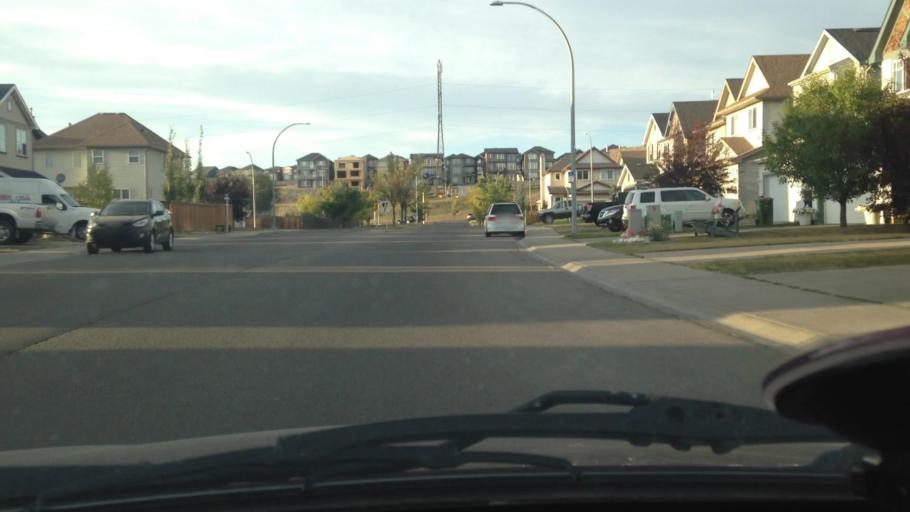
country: CA
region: Alberta
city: Calgary
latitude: 51.1661
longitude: -114.1214
